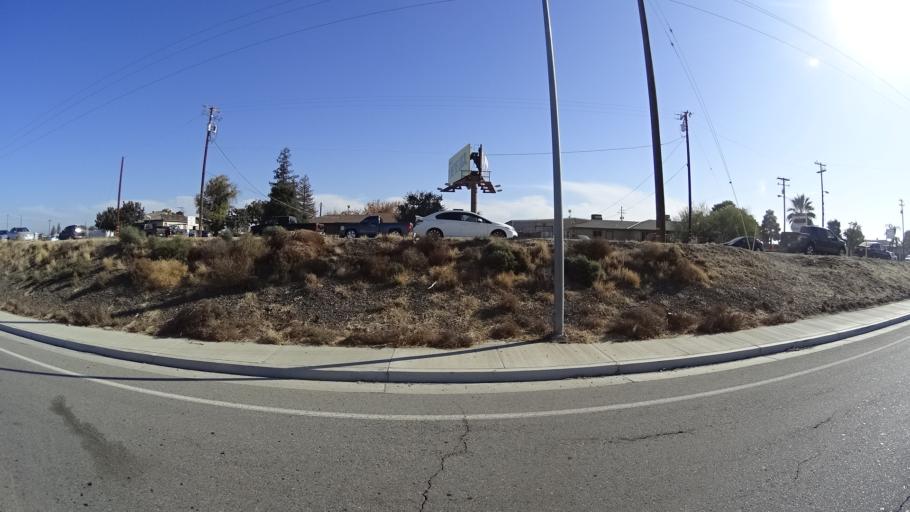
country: US
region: California
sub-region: Kern County
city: Rosedale
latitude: 35.3961
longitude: -119.1458
